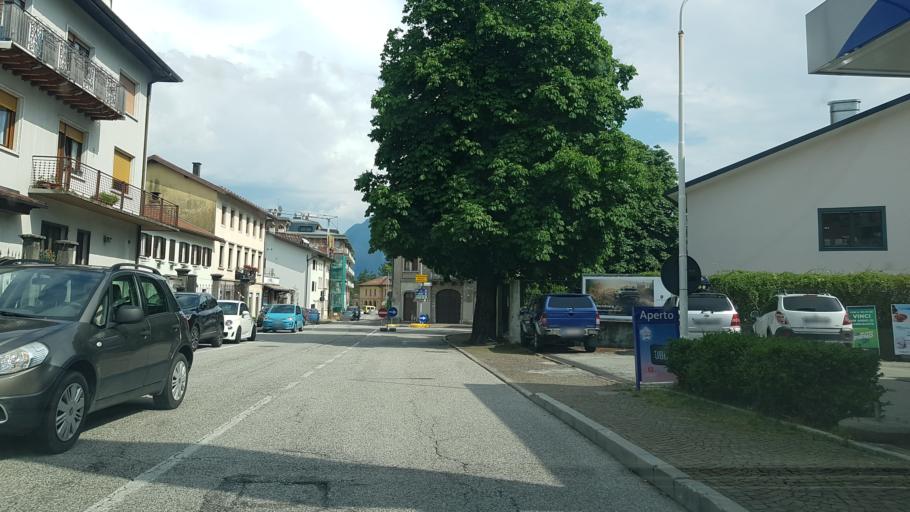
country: IT
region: Friuli Venezia Giulia
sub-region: Provincia di Udine
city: Tolmezzo
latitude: 46.4029
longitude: 13.0174
